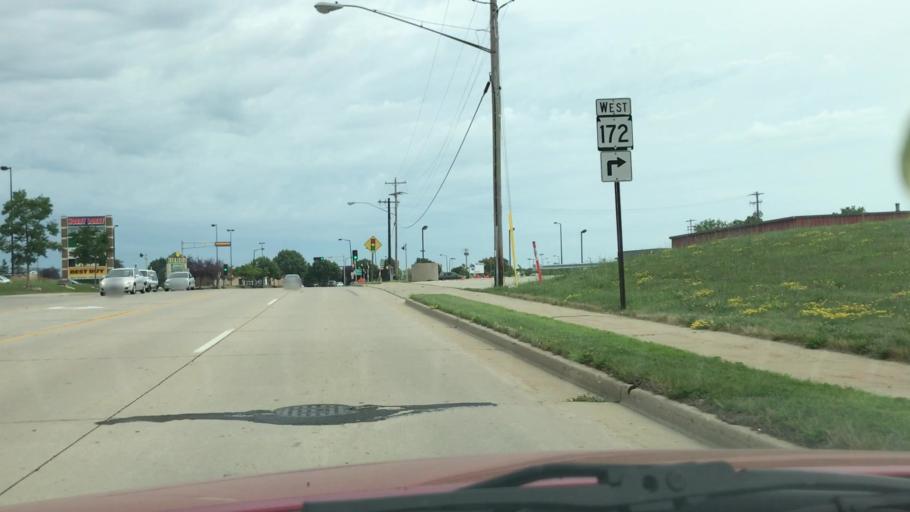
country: US
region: Wisconsin
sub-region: Brown County
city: Ashwaubenon
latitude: 44.4801
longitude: -88.0663
